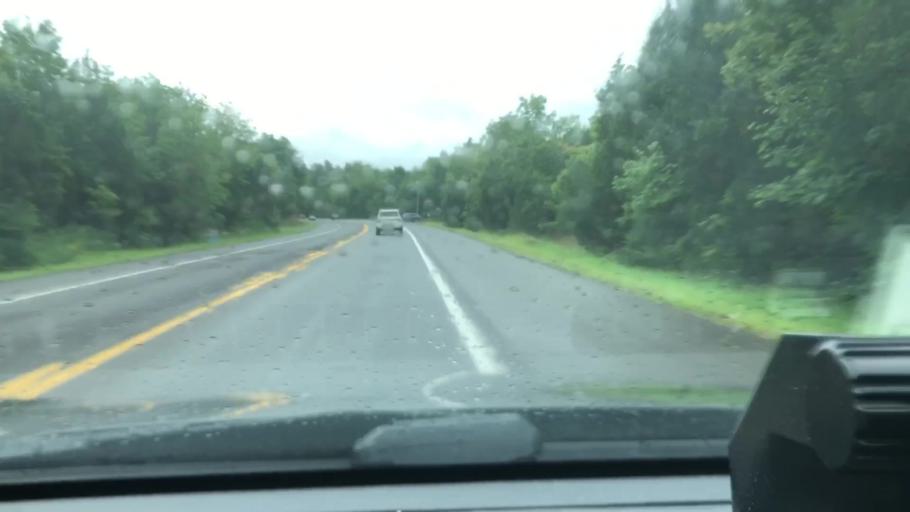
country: US
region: Pennsylvania
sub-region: Montgomery County
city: Pennsburg
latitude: 40.4129
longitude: -75.4639
